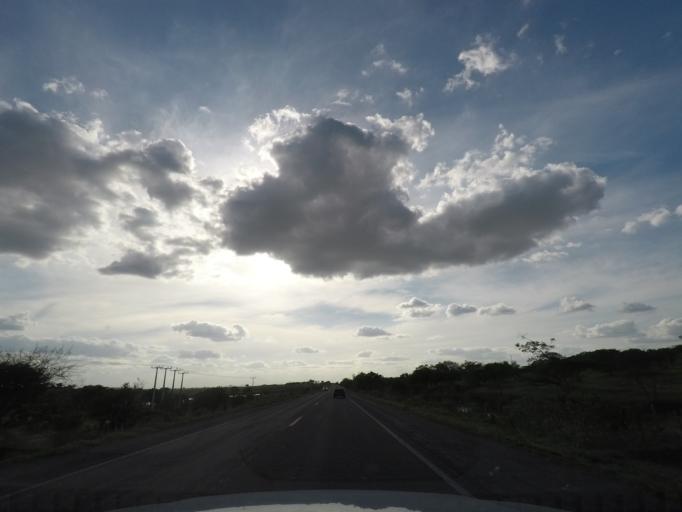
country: BR
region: Bahia
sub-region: Anguera
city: Anguera
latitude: -12.1858
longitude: -39.4814
